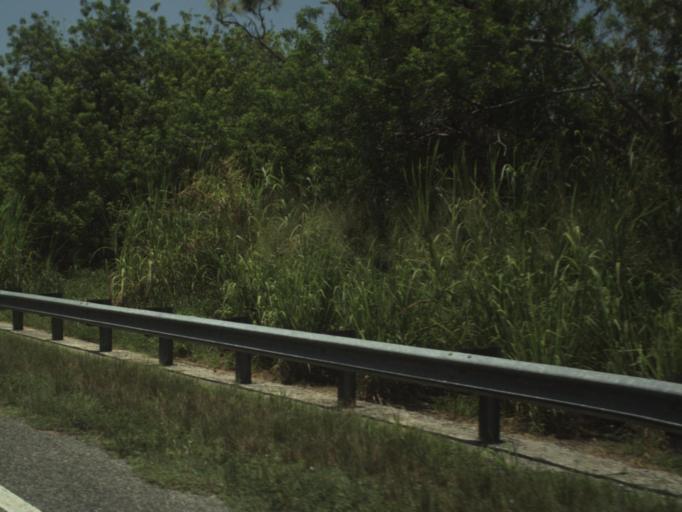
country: US
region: Florida
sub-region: Martin County
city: Indiantown
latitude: 27.0289
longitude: -80.4116
